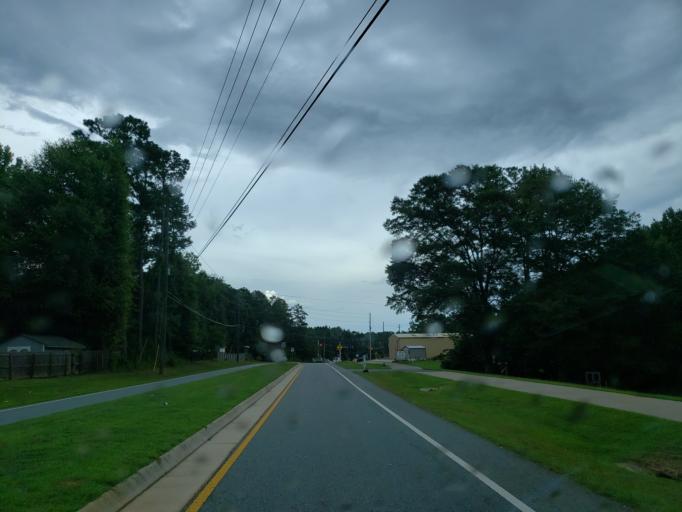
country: US
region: Georgia
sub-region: Cobb County
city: Acworth
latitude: 34.0309
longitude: -84.7440
